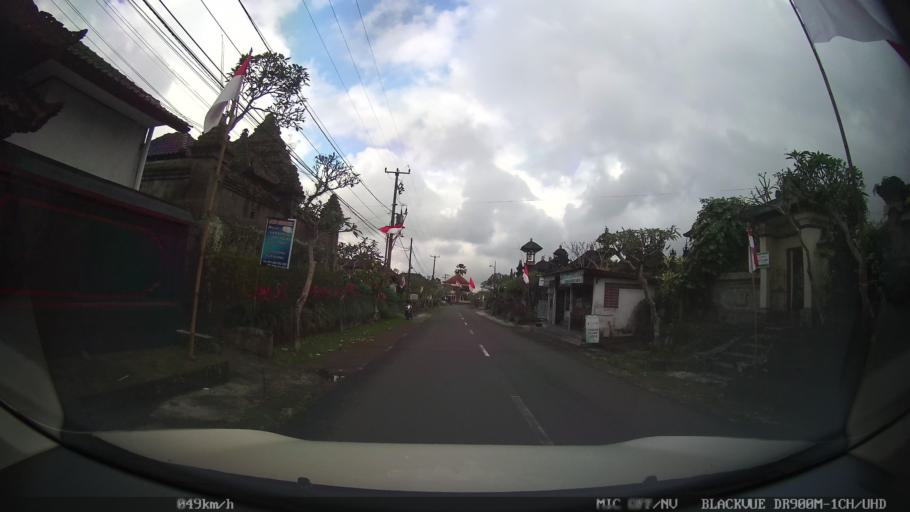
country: ID
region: Bali
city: Peneng
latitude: -8.3686
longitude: 115.1783
